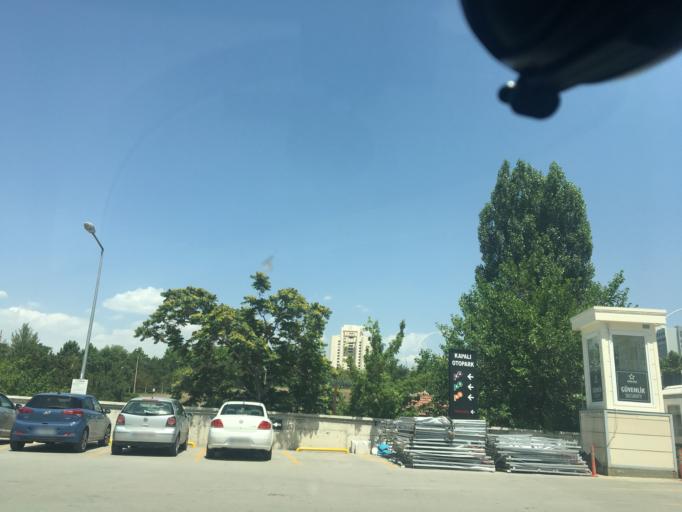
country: TR
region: Ankara
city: Ankara
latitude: 39.9123
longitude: 32.8112
